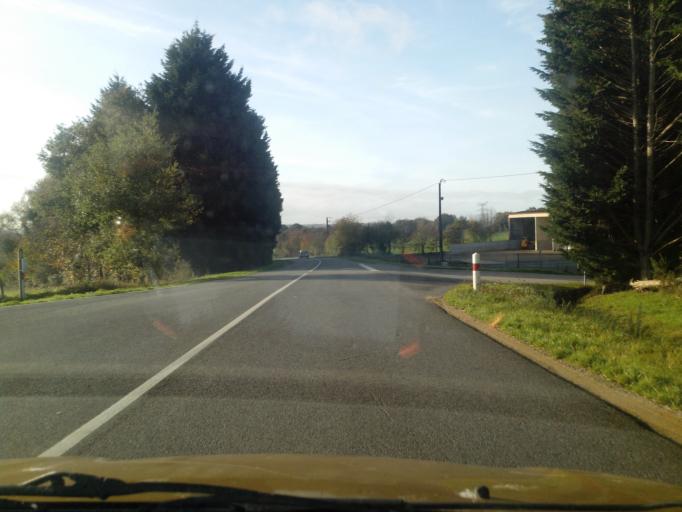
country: FR
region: Brittany
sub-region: Departement du Morbihan
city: Josselin
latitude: 47.9733
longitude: -2.5450
